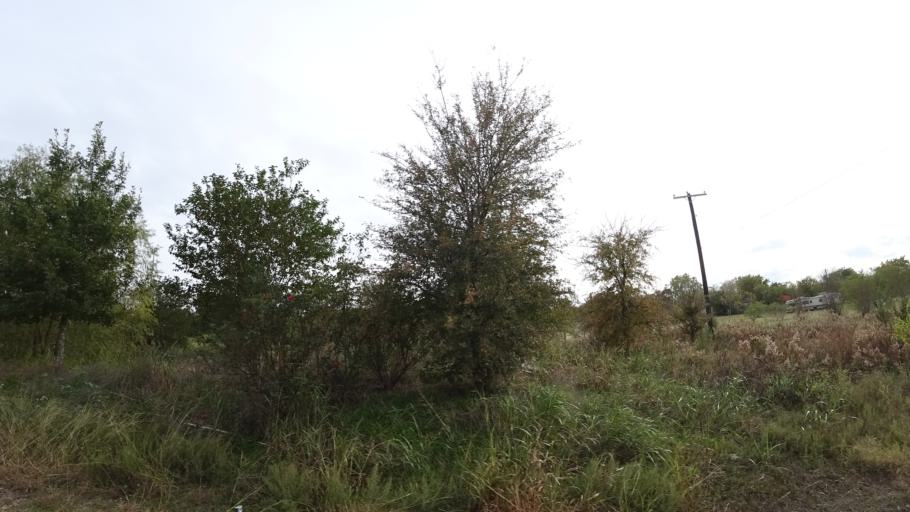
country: US
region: Texas
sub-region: Williamson County
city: Round Rock
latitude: 30.4997
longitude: -97.6581
